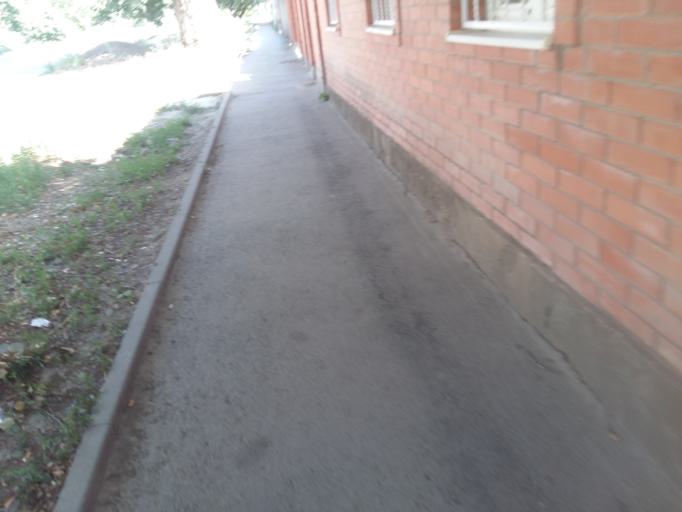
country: RU
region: Rostov
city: Imeni Chkalova
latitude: 47.2767
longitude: 39.7450
